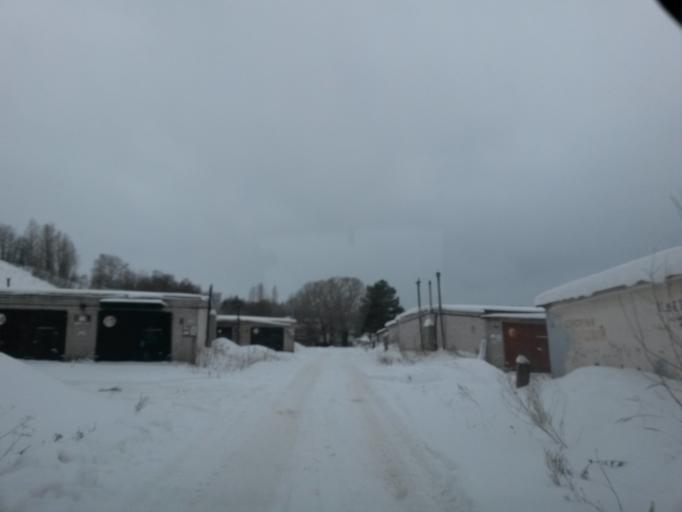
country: RU
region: Jaroslavl
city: Yaroslavl
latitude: 57.5752
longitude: 39.8397
